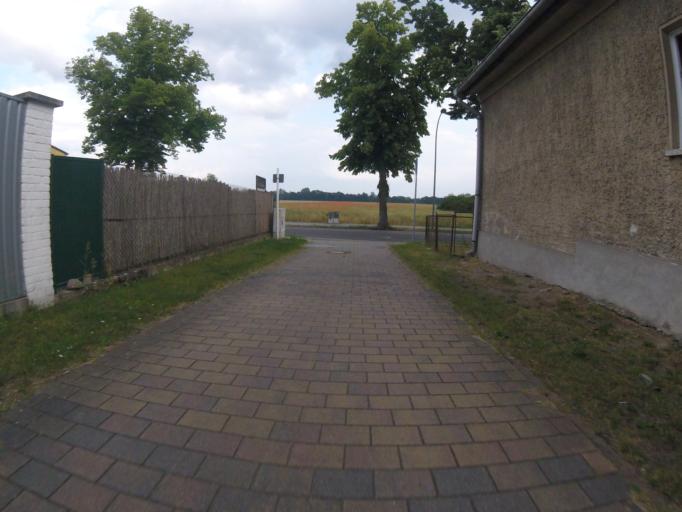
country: DE
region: Brandenburg
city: Konigs Wusterhausen
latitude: 52.2955
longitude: 13.5890
